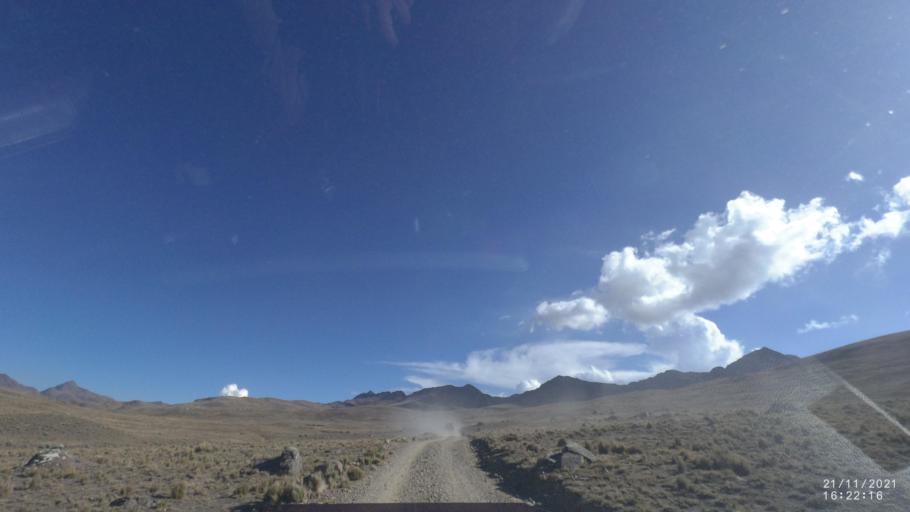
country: BO
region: Cochabamba
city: Cochabamba
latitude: -17.0180
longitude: -66.2856
